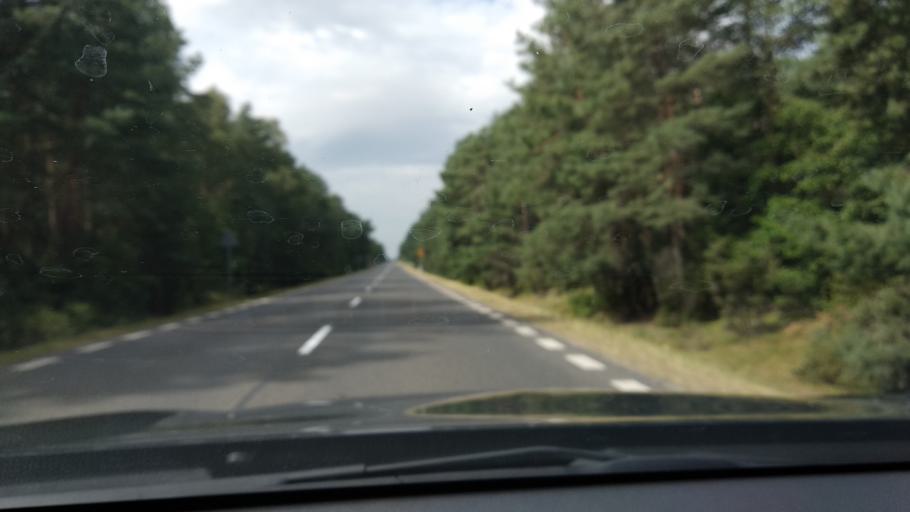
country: PL
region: Masovian Voivodeship
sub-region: Powiat pultuski
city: Zatory
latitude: 52.5442
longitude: 21.1525
